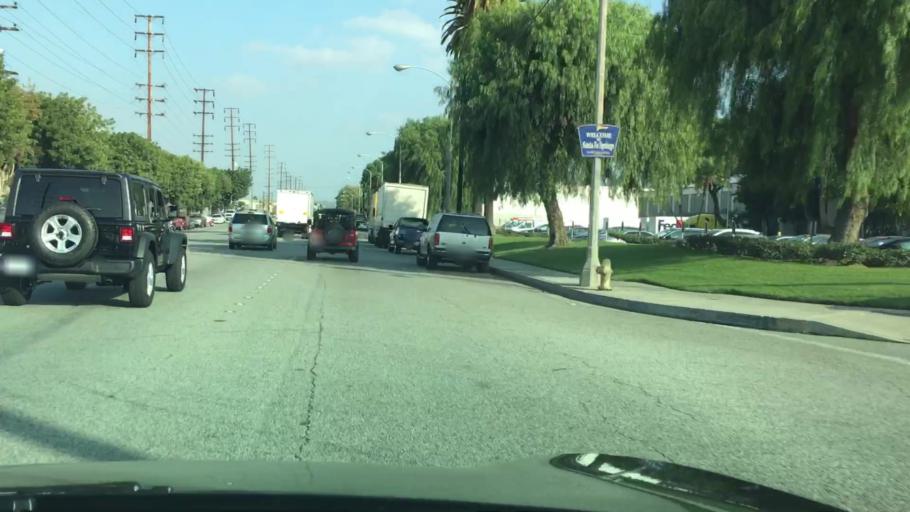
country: US
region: California
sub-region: Los Angeles County
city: La Mirada
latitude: 33.9024
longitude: -118.0443
